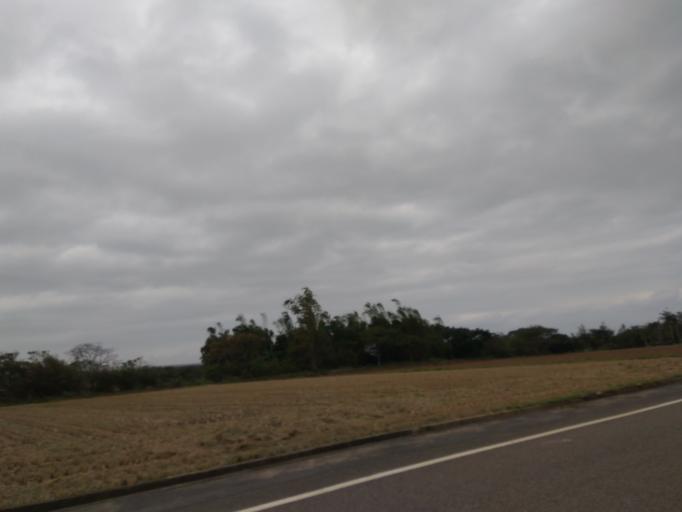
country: TW
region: Taiwan
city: Taoyuan City
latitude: 25.0320
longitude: 121.2204
